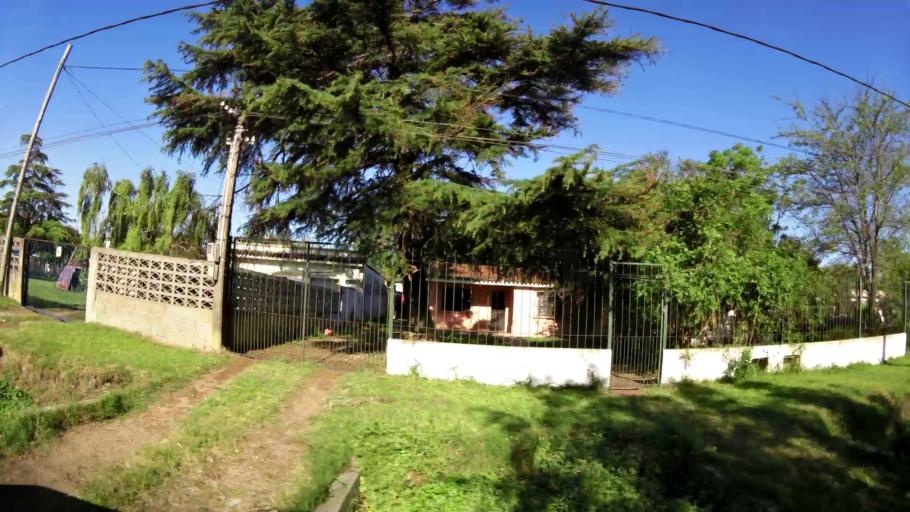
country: UY
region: Canelones
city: La Paz
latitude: -34.8206
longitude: -56.1741
